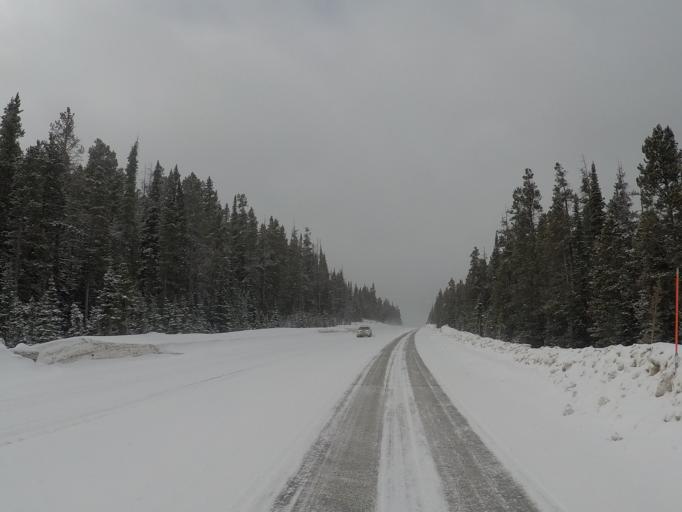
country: US
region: Montana
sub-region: Meagher County
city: White Sulphur Springs
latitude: 46.8467
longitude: -110.6907
